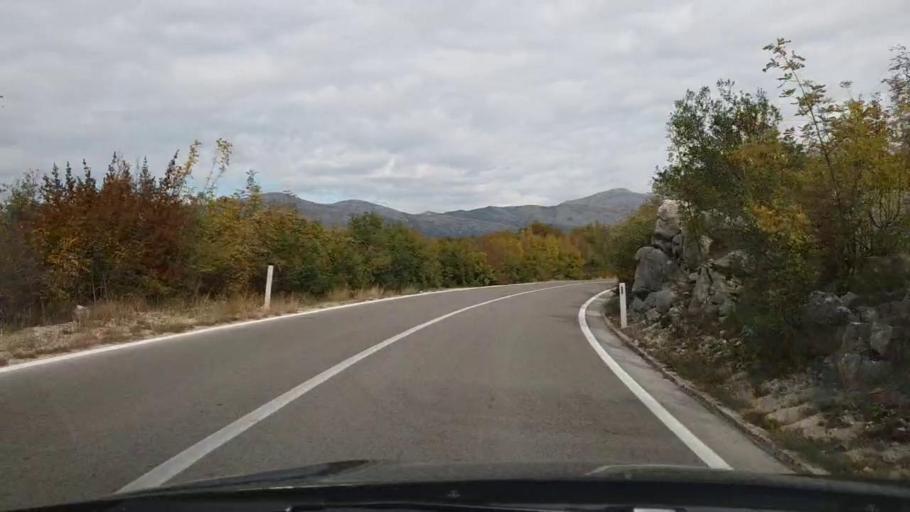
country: HR
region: Dubrovacko-Neretvanska
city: Jasenice
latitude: 42.6856
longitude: 18.2481
